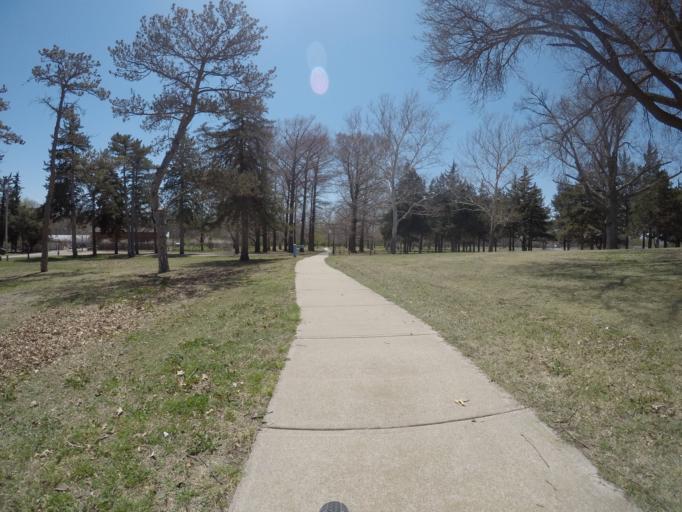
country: US
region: Kansas
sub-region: Pratt County
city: Pratt
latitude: 37.6389
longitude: -98.7307
